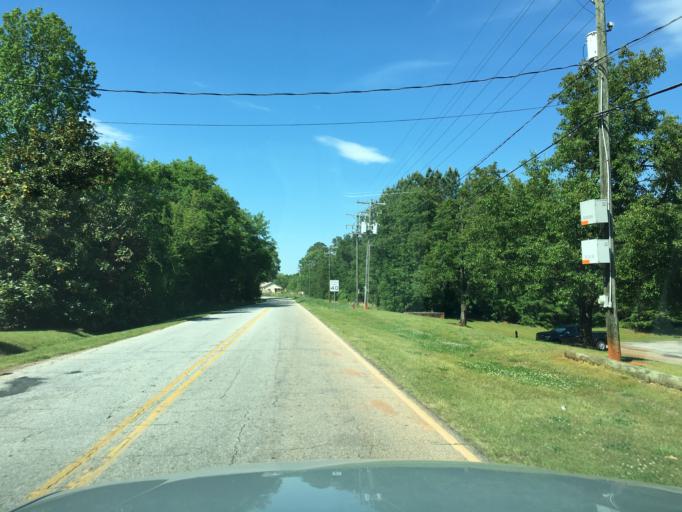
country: US
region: South Carolina
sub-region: Spartanburg County
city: Fairforest
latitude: 34.9788
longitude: -82.0321
